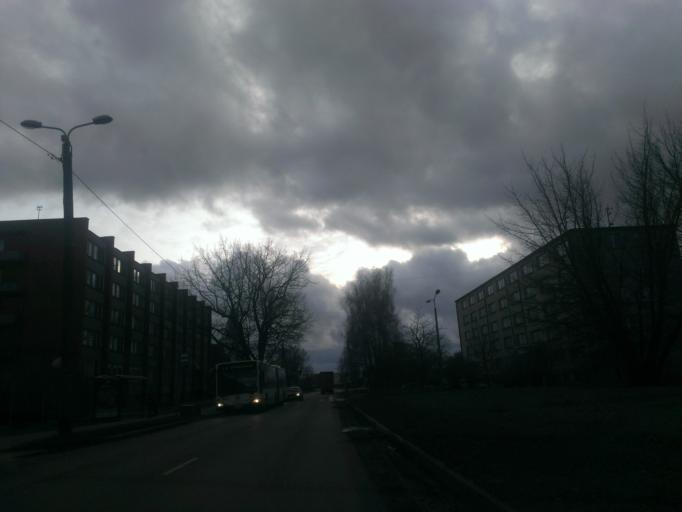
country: LV
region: Riga
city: Bolderaja
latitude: 57.0381
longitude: 24.0874
